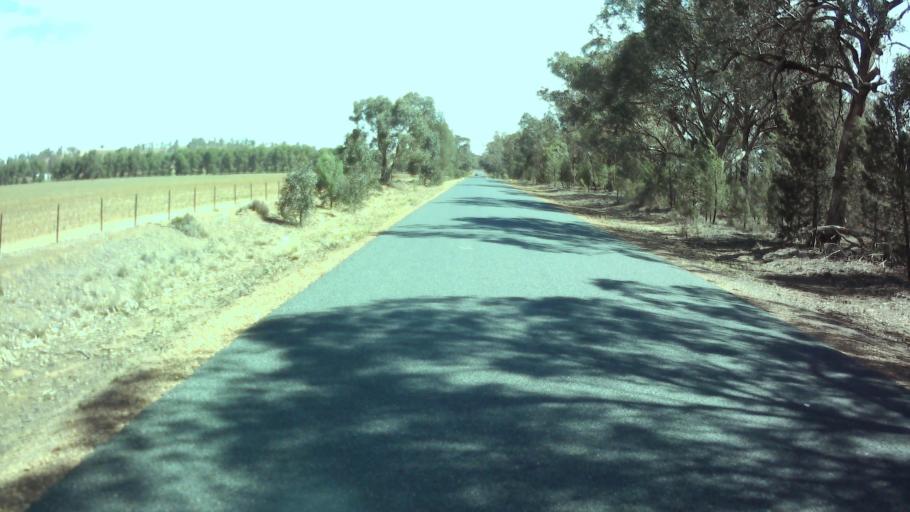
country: AU
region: New South Wales
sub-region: Weddin
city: Grenfell
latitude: -34.0392
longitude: 148.1344
